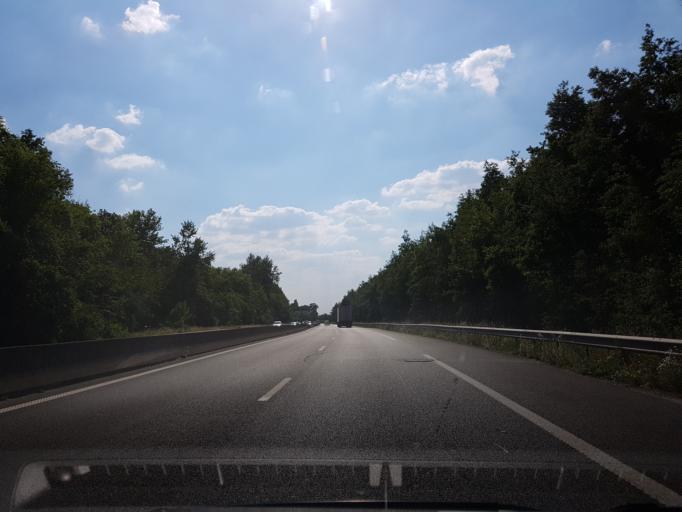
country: FR
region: Nord-Pas-de-Calais
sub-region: Departement du Nord
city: Montigny-en-Ostrevent
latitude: 50.3824
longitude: 3.1925
